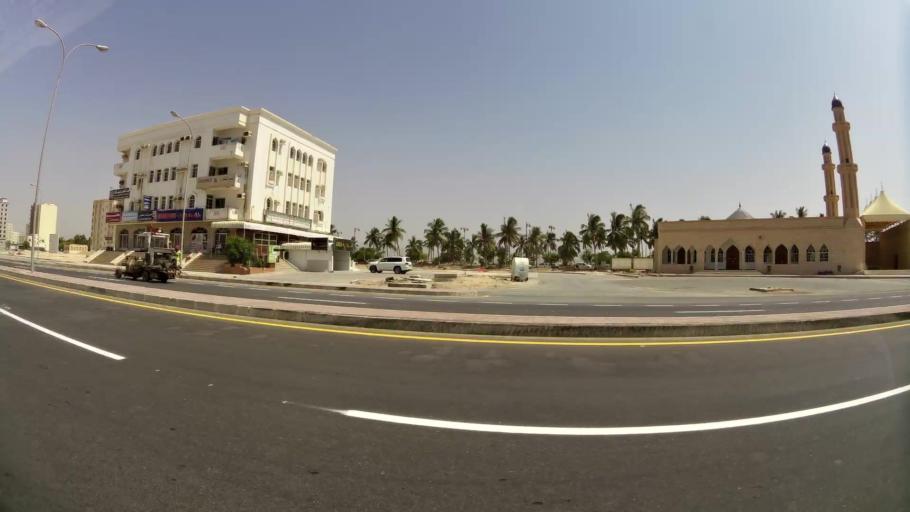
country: OM
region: Zufar
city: Salalah
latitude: 17.0223
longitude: 54.1003
